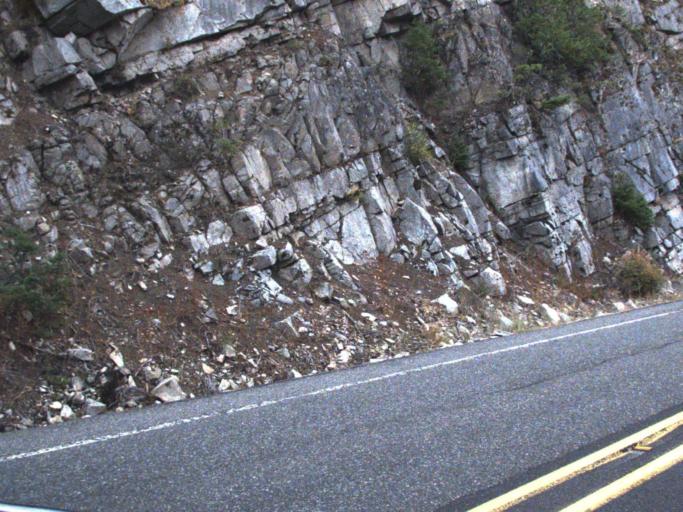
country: US
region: Washington
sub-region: Yakima County
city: Tieton
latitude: 46.6562
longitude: -121.4729
